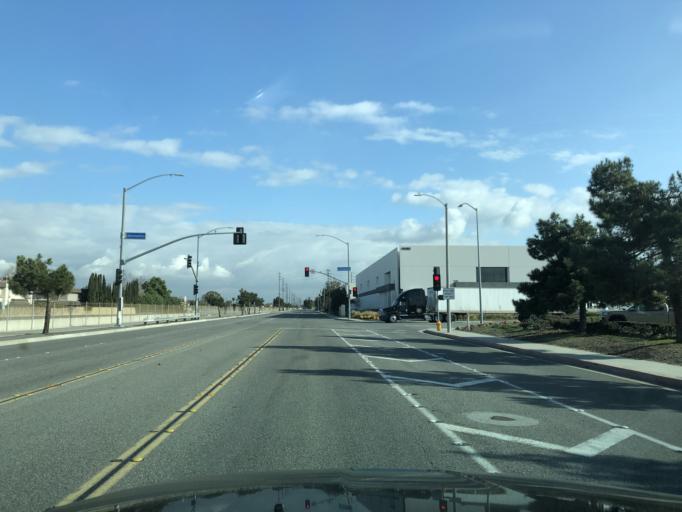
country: US
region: California
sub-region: Orange County
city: Westminster
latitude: 33.7518
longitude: -118.0395
